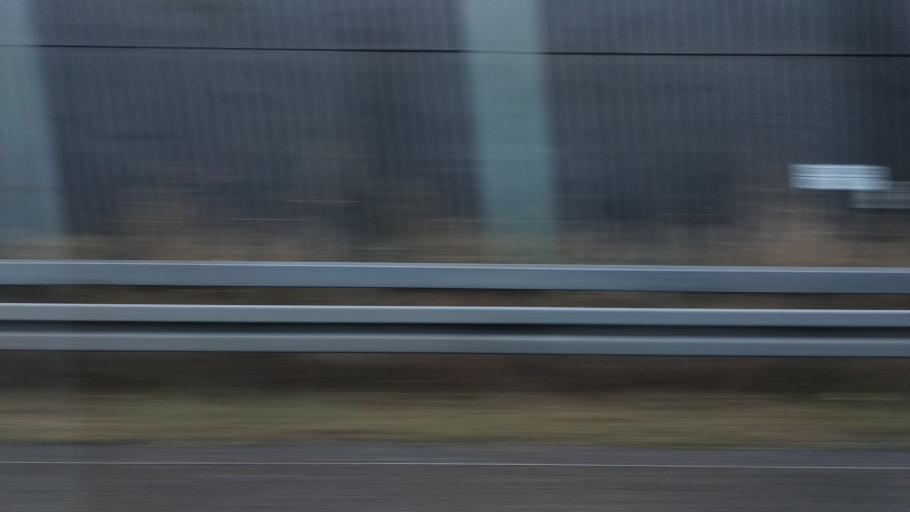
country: DE
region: Bavaria
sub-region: Swabia
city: Weissensberg
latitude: 47.5675
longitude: 9.7368
